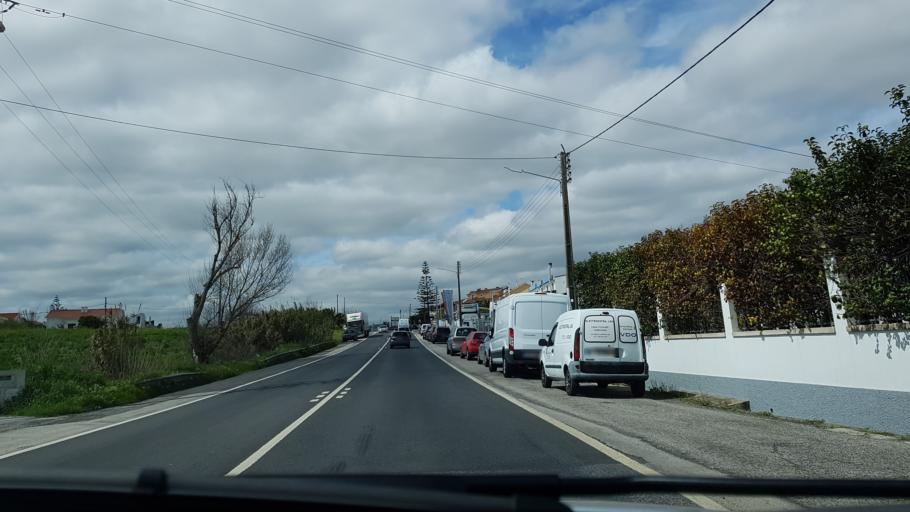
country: PT
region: Lisbon
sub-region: Alenquer
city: Carregado
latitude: 39.0330
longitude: -8.9511
